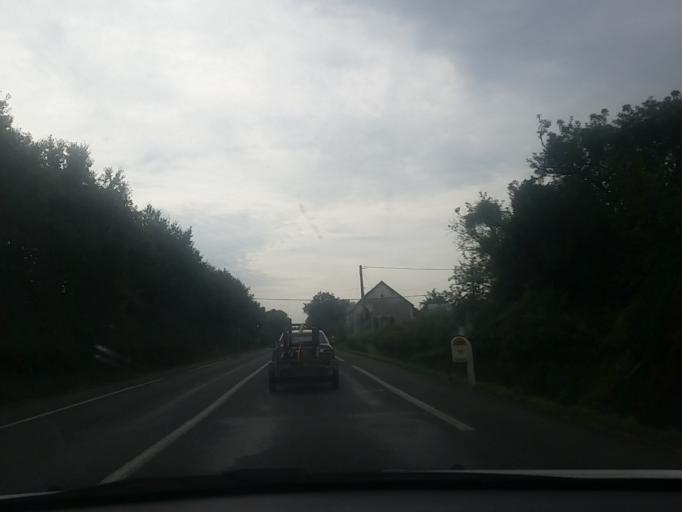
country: FR
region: Pays de la Loire
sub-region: Departement de la Vendee
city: Chavagnes-en-Paillers
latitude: 46.8981
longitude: -1.2284
